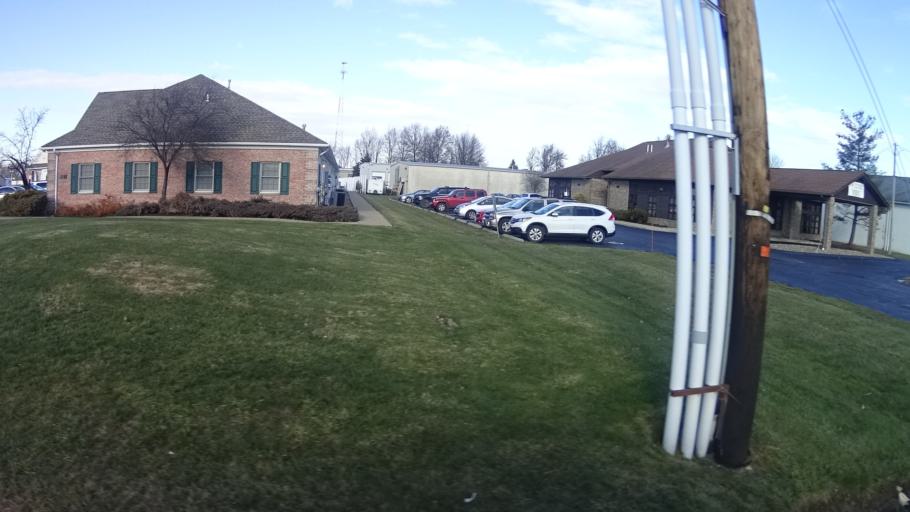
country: US
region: Ohio
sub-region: Lorain County
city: Elyria
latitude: 41.3630
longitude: -82.0720
